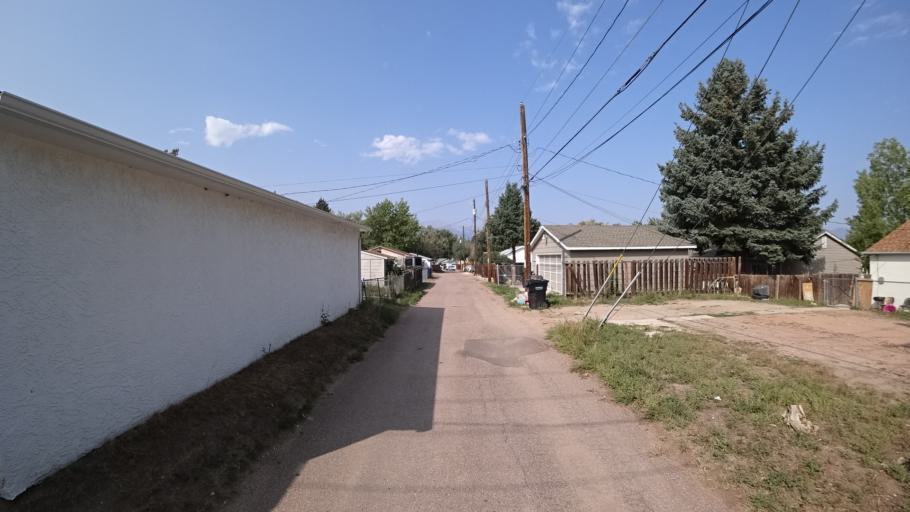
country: US
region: Colorado
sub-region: El Paso County
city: Colorado Springs
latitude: 38.8503
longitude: -104.7807
